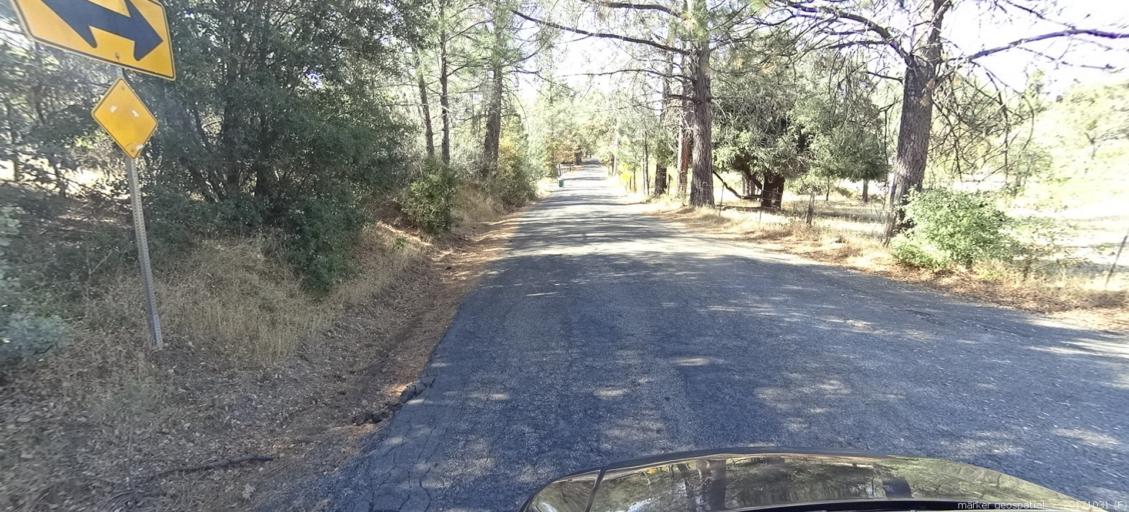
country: US
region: California
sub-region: Shasta County
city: Shingletown
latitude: 40.5241
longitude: -121.9571
